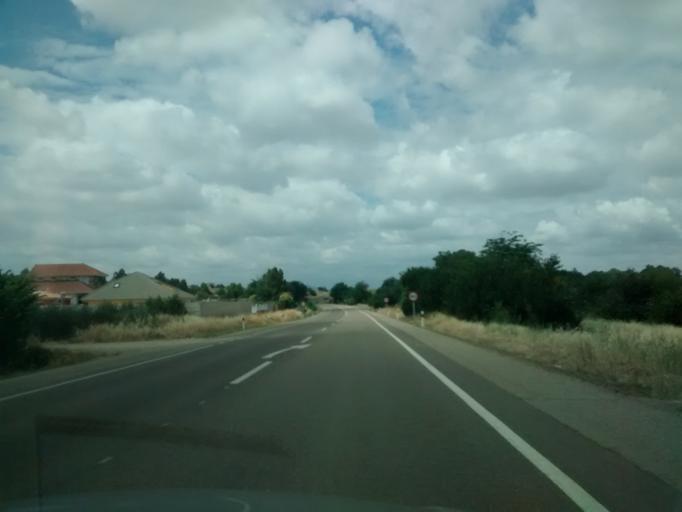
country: ES
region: Extremadura
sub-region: Provincia de Badajoz
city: Merida
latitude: 38.9373
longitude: -6.3029
